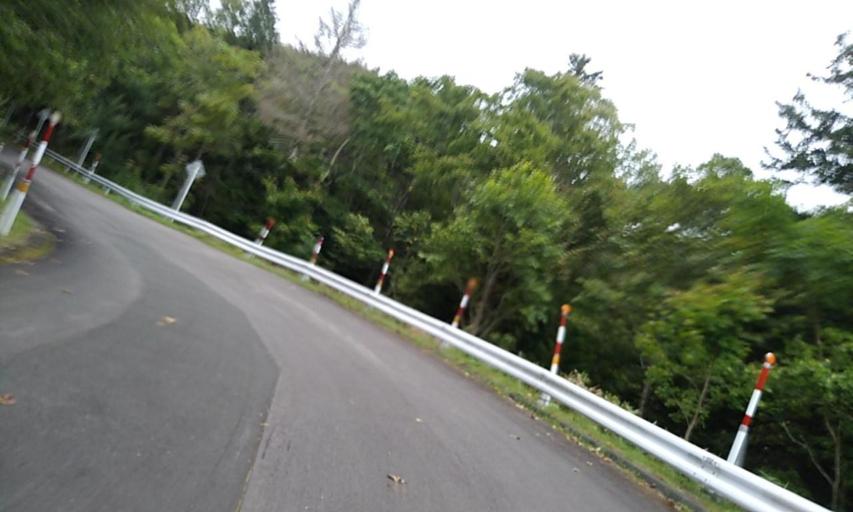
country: JP
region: Hokkaido
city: Bihoro
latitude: 43.5676
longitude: 144.1933
